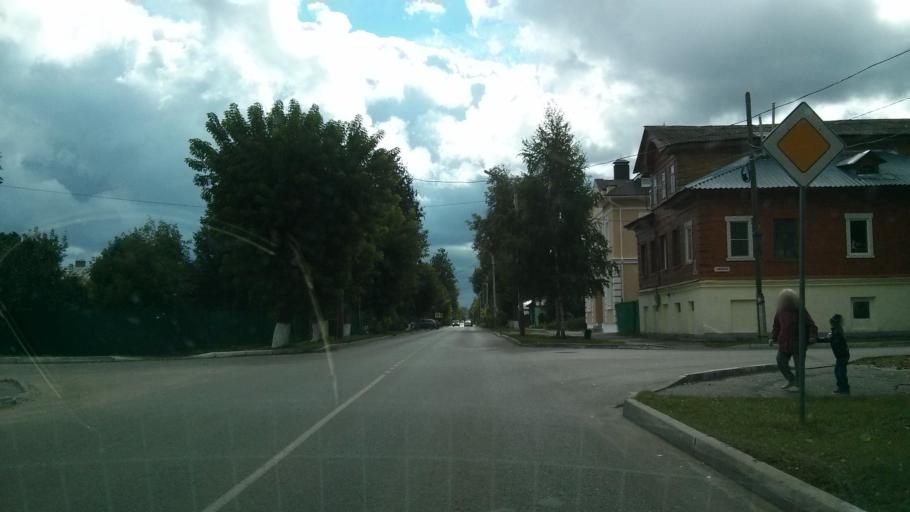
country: RU
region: Vladimir
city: Murom
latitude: 55.5742
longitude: 42.0609
